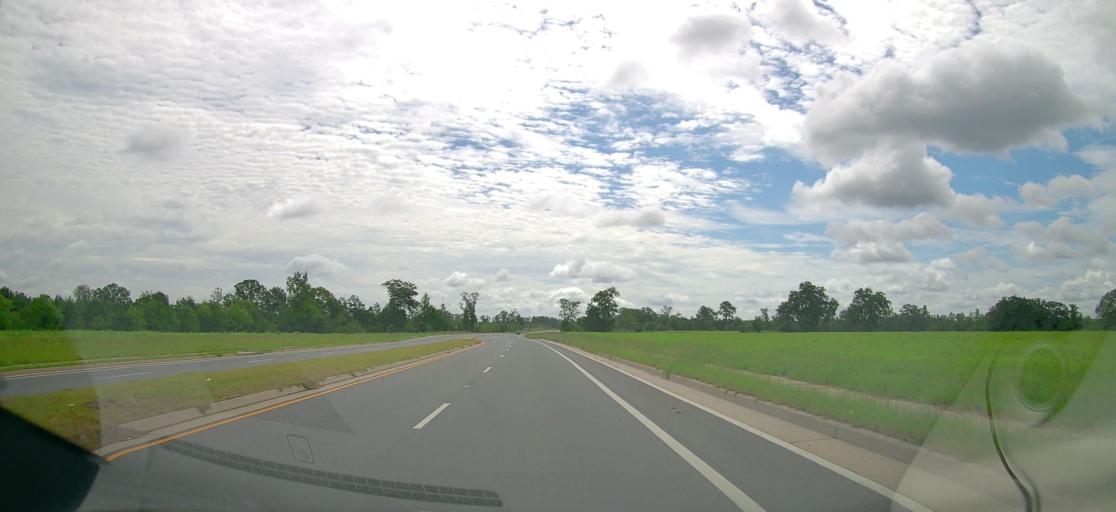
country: US
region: Georgia
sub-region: Houston County
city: Centerville
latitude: 32.6833
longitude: -83.6732
